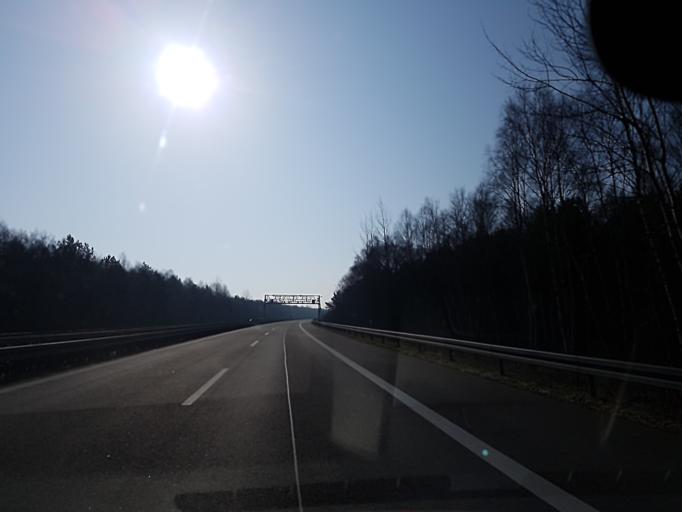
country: DE
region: Brandenburg
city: Forst
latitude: 51.7002
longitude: 14.6545
